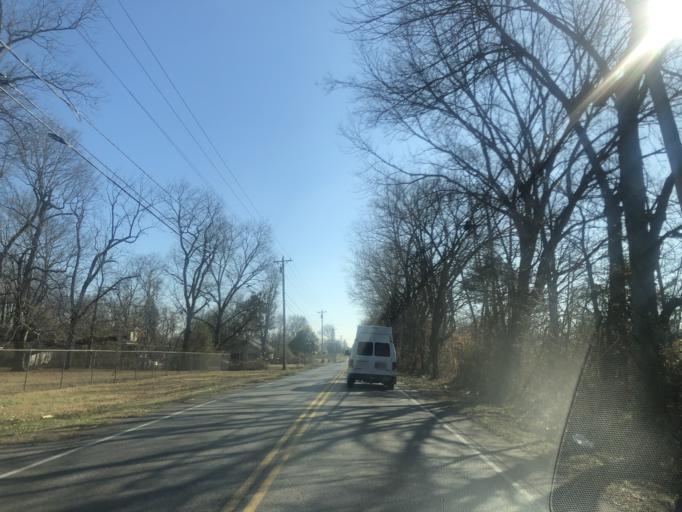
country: US
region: Tennessee
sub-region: Rutherford County
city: Smyrna
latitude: 35.9181
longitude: -86.4749
